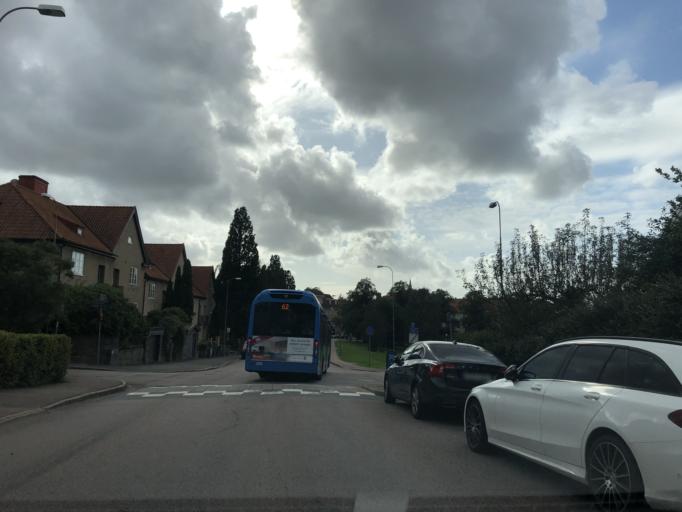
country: SE
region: Vaestra Goetaland
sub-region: Goteborg
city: Goeteborg
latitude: 57.7210
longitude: 12.0104
